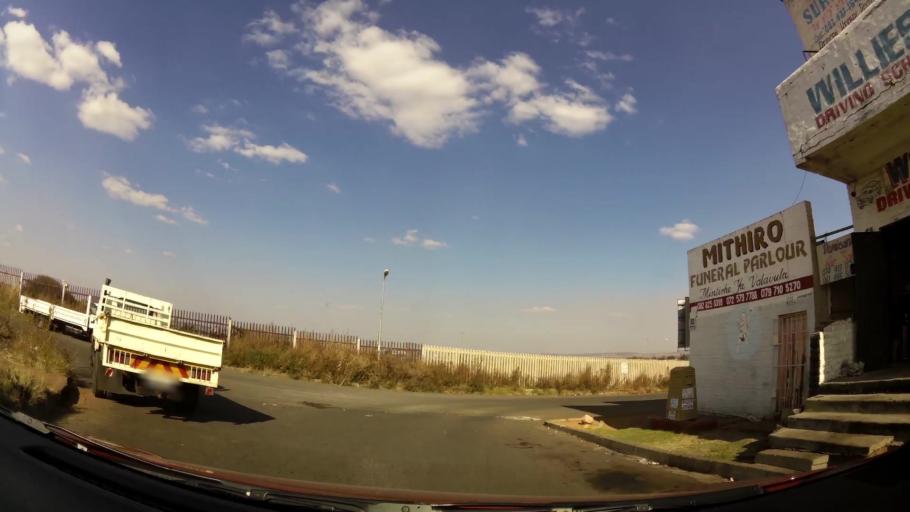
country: ZA
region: Gauteng
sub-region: City of Johannesburg Metropolitan Municipality
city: Soweto
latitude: -26.2318
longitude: 27.8754
